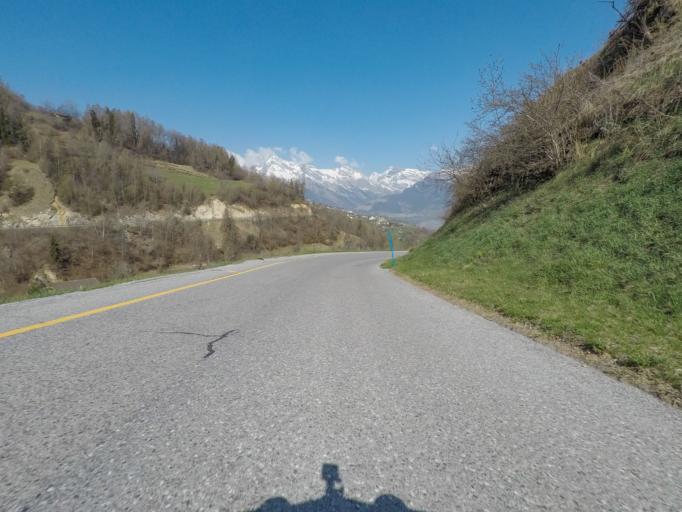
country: CH
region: Valais
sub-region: Conthey District
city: Basse-Nendaz
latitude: 46.1826
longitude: 7.3260
